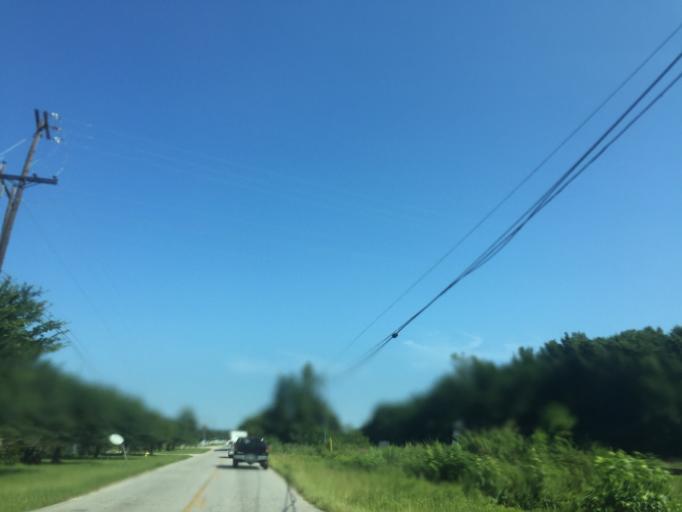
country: US
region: Georgia
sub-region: Chatham County
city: Garden City
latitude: 32.0768
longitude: -81.1445
